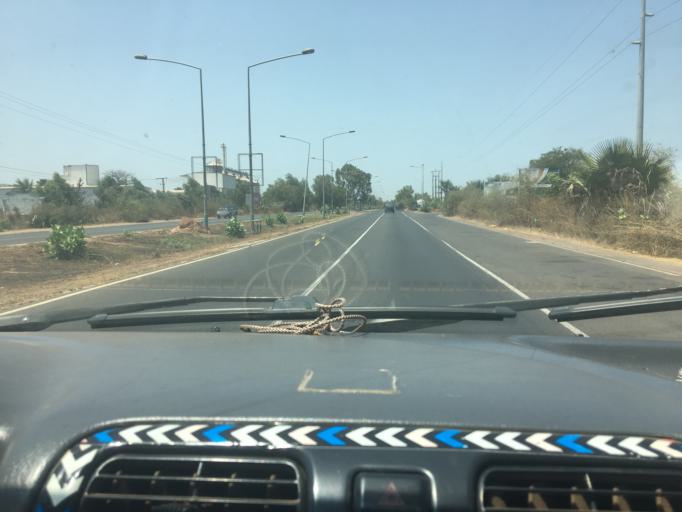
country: GM
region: Banjul
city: Bakau
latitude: 13.4670
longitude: -16.6502
